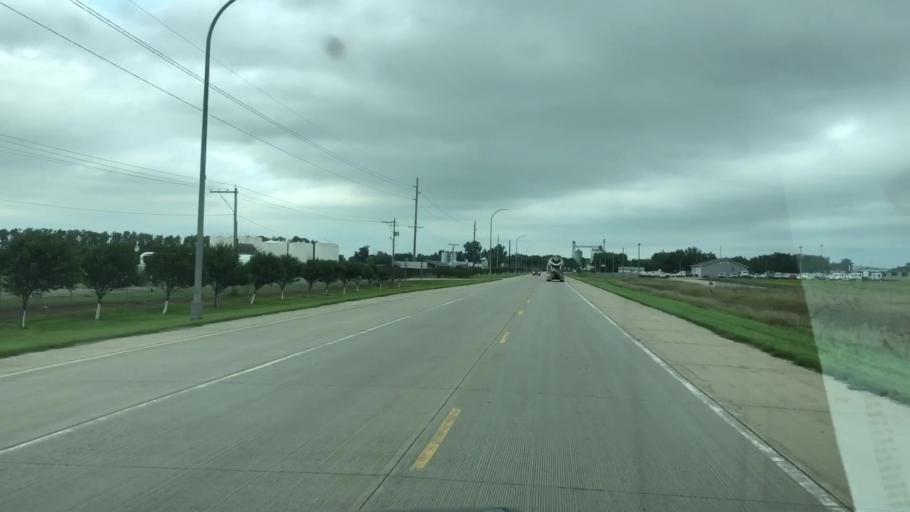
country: US
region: Iowa
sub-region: O'Brien County
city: Sheldon
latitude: 43.1623
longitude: -95.8613
